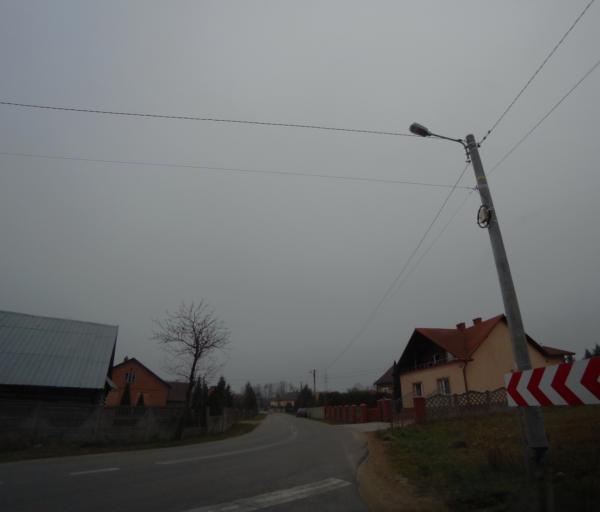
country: PL
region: Subcarpathian Voivodeship
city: Nowa Sarzyna
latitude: 50.2904
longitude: 22.3528
